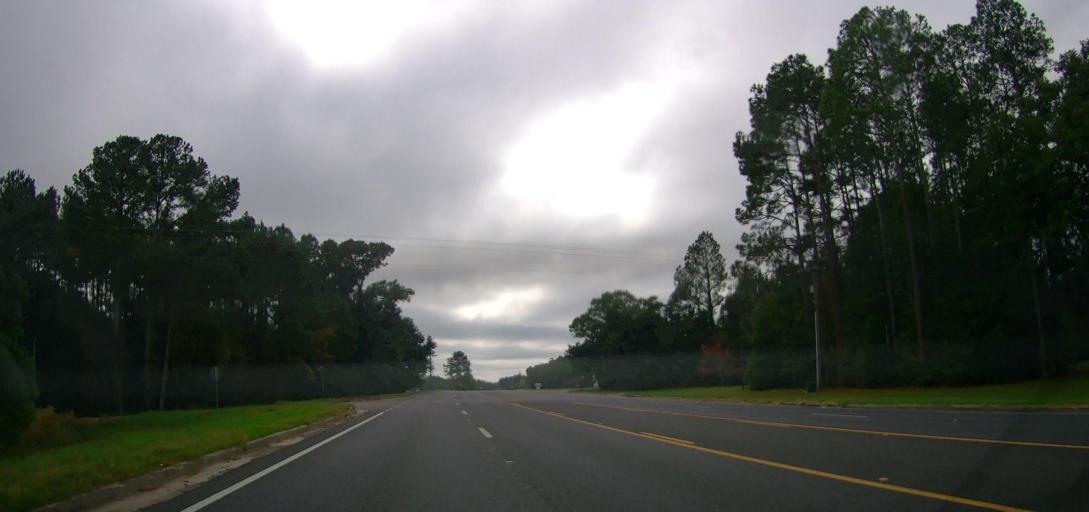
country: US
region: Georgia
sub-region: Colquitt County
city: Moultrie
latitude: 31.0725
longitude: -83.8229
